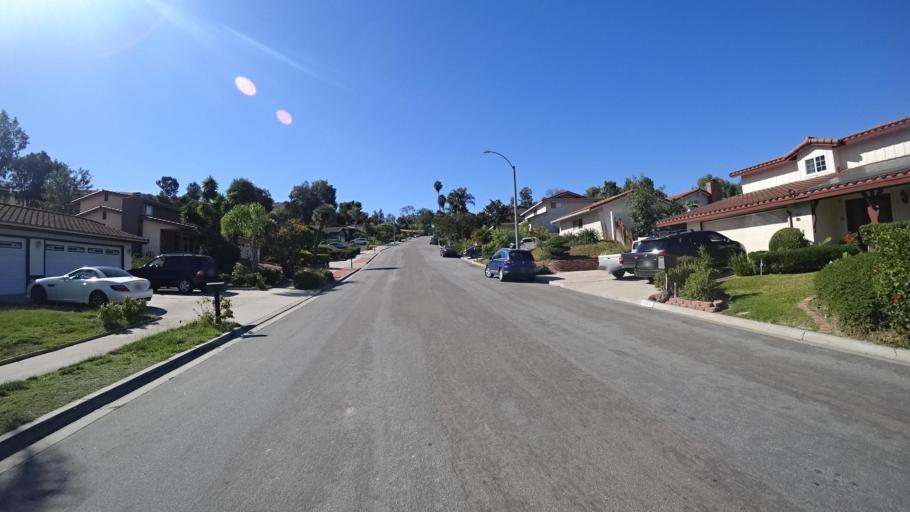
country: US
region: California
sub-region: San Diego County
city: Bonita
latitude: 32.6682
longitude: -117.0085
